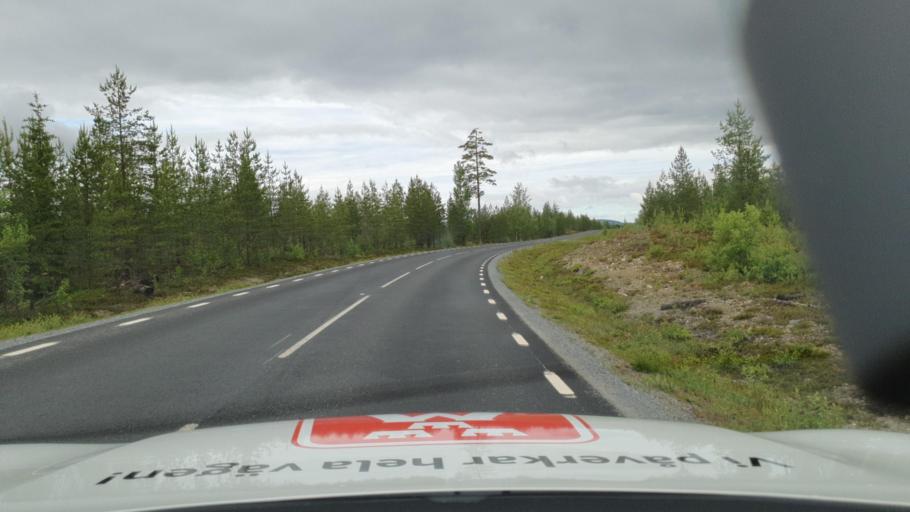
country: SE
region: Vaesterbotten
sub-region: Dorotea Kommun
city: Dorotea
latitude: 64.1908
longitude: 16.5955
